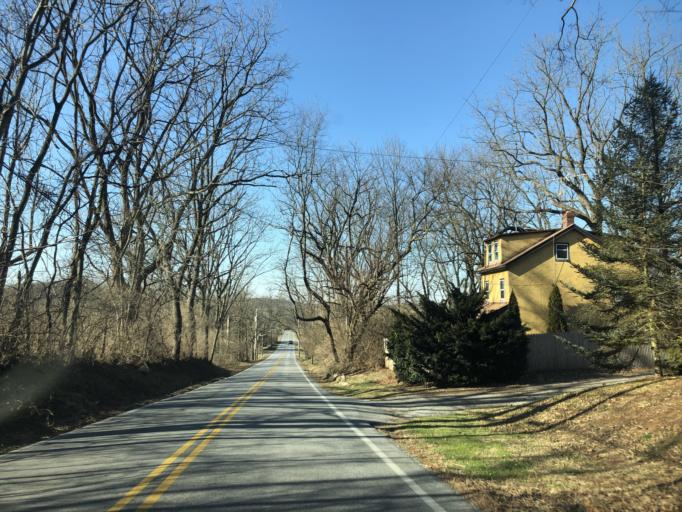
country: US
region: Pennsylvania
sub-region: Chester County
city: Upland
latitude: 39.9003
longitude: -75.7668
